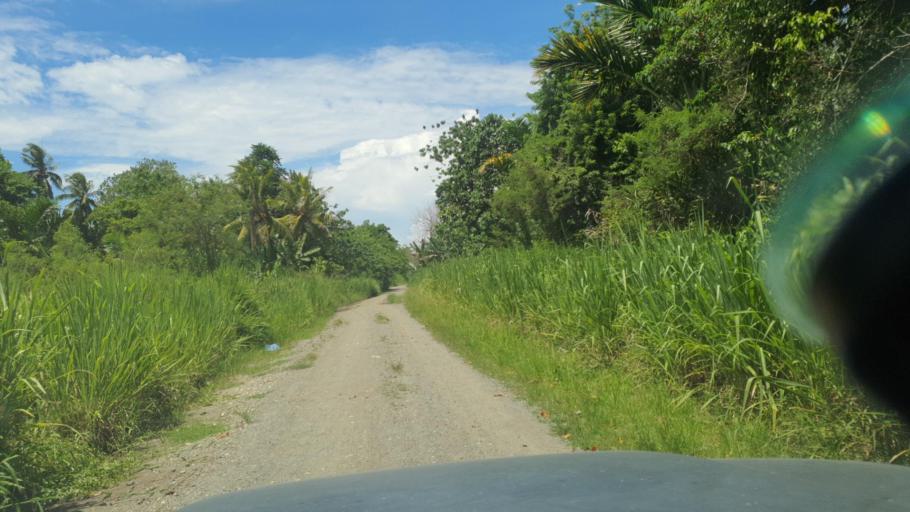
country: SB
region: Guadalcanal
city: Honiara
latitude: -9.4240
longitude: 160.1813
